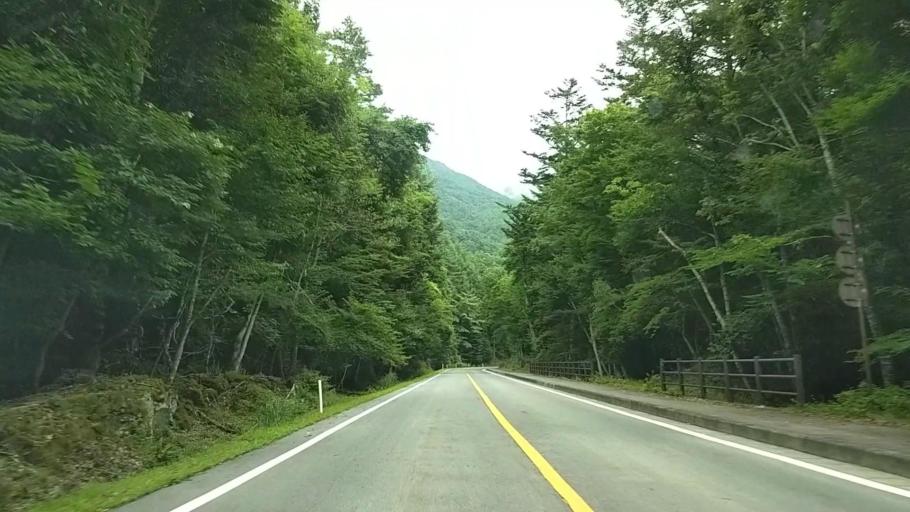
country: JP
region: Yamanashi
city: Fujikawaguchiko
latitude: 35.4950
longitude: 138.6492
